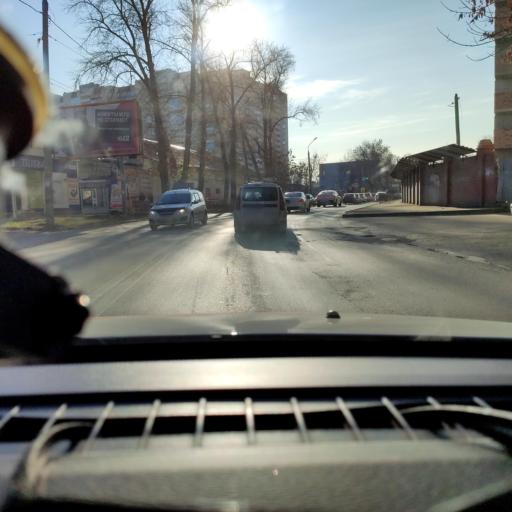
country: RU
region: Samara
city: Samara
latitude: 53.2063
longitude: 50.1777
